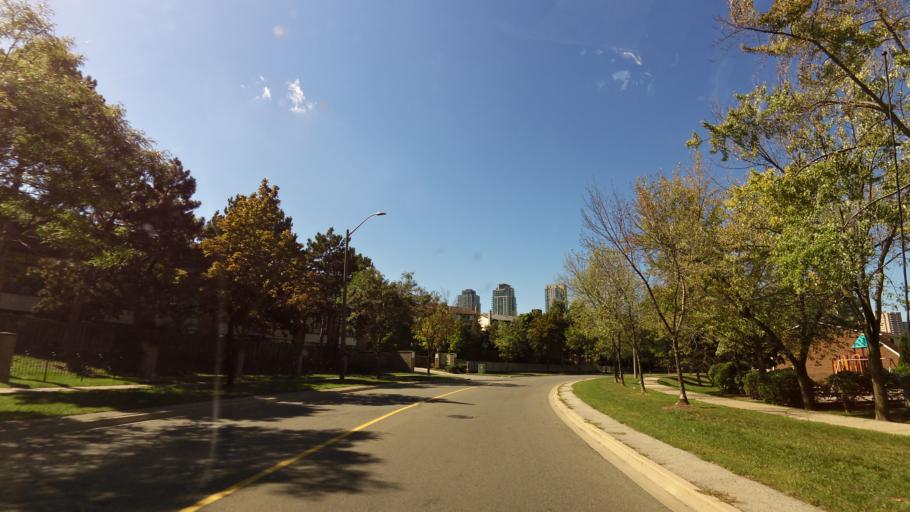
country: CA
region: Ontario
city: Mississauga
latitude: 43.5873
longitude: -79.6226
